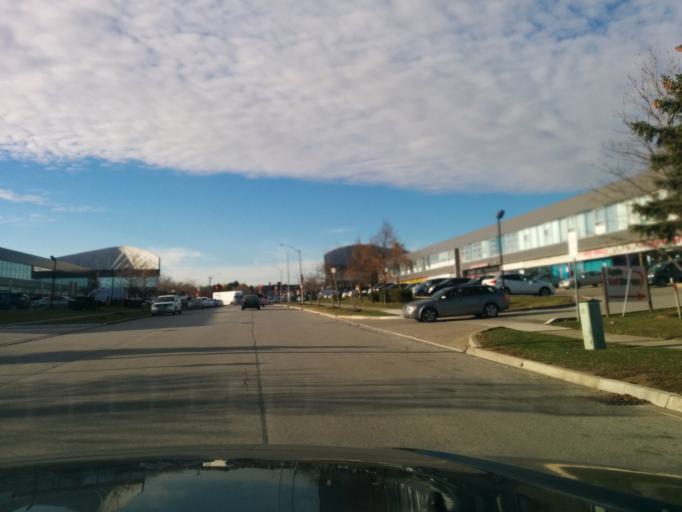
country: CA
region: Ontario
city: Etobicoke
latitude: 43.6132
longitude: -79.5764
